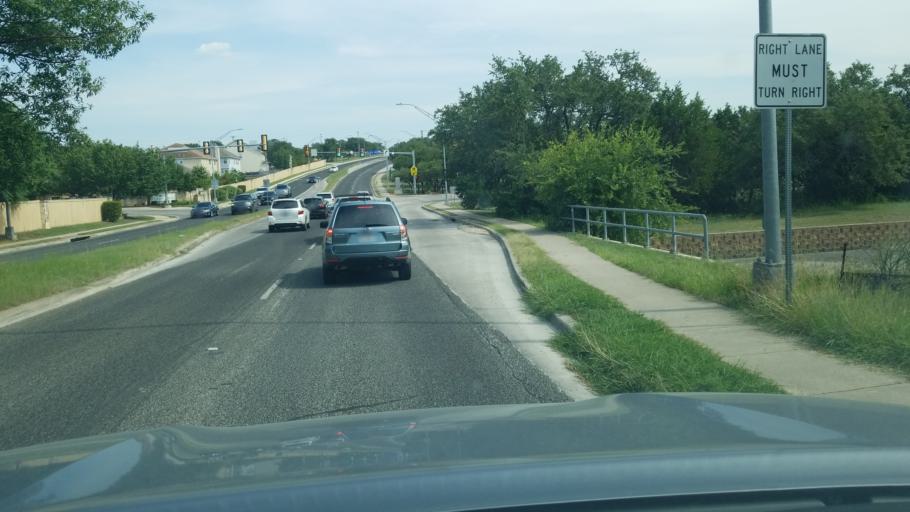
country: US
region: Texas
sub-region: Bexar County
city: Timberwood Park
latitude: 29.6588
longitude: -98.4973
